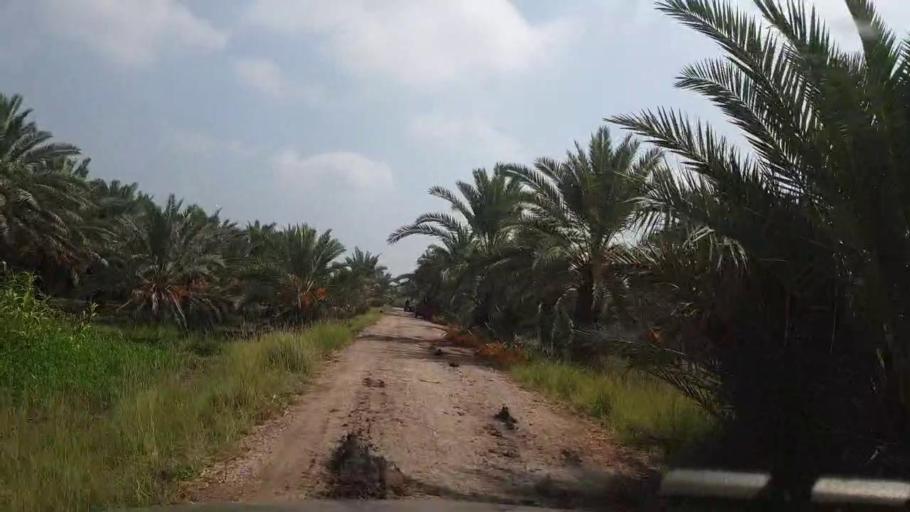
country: PK
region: Sindh
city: Pir jo Goth
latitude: 27.6027
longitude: 68.6953
